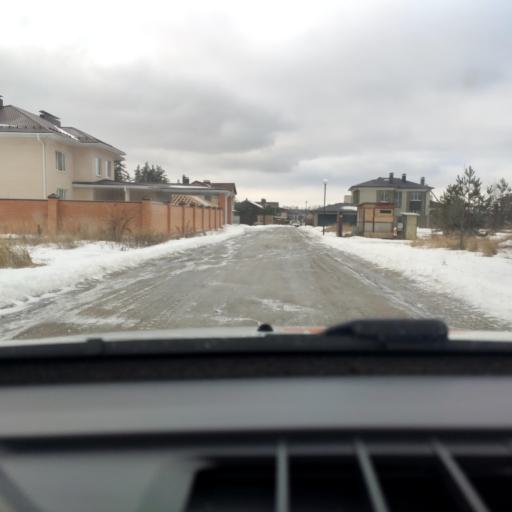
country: RU
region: Voronezj
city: Podgornoye
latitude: 51.7539
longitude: 39.1444
